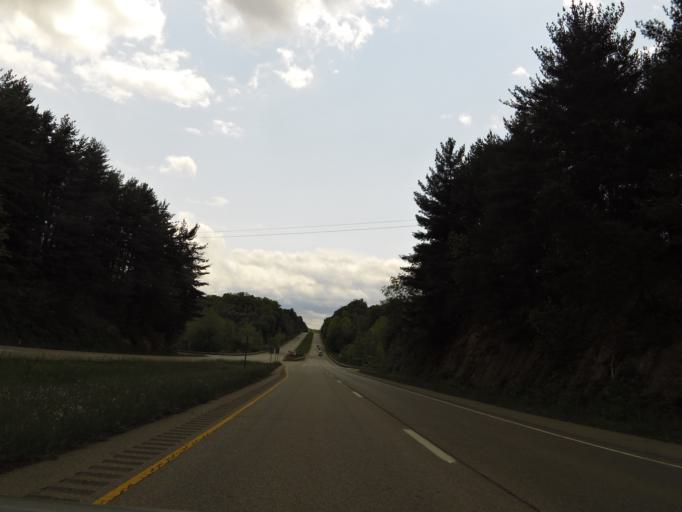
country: US
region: Ohio
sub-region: Meigs County
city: Pomeroy
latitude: 39.1153
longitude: -82.0160
